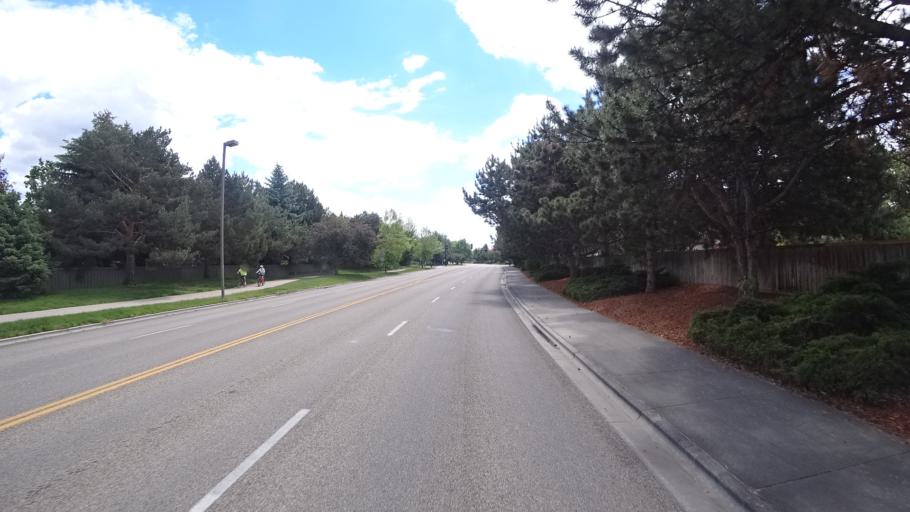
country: US
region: Idaho
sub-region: Ada County
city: Boise
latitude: 43.5816
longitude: -116.1638
